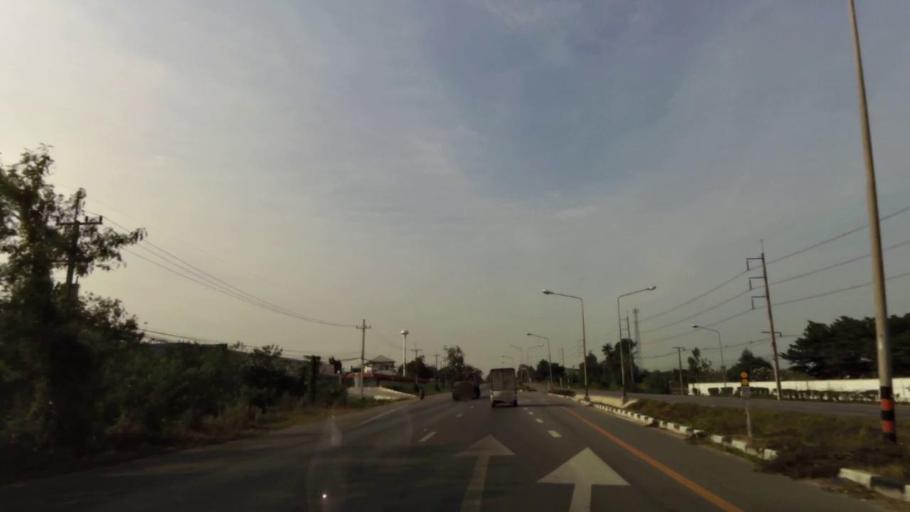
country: TH
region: Chon Buri
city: Ban Bueng
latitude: 13.2579
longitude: 101.2009
